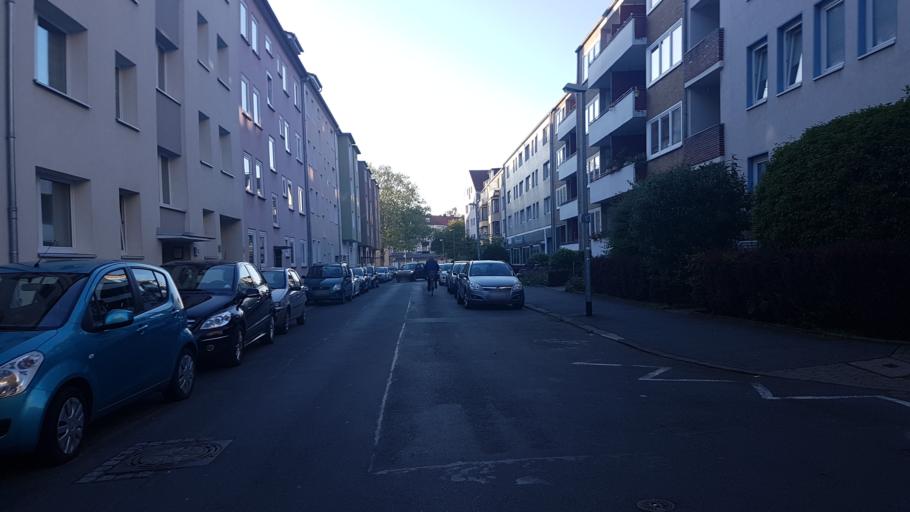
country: DE
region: Lower Saxony
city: Hannover
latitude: 52.3857
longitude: 9.7373
